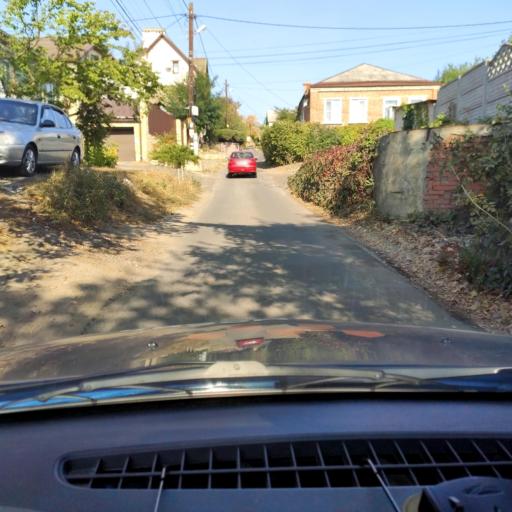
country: RU
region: Voronezj
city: Voronezh
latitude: 51.6867
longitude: 39.2243
